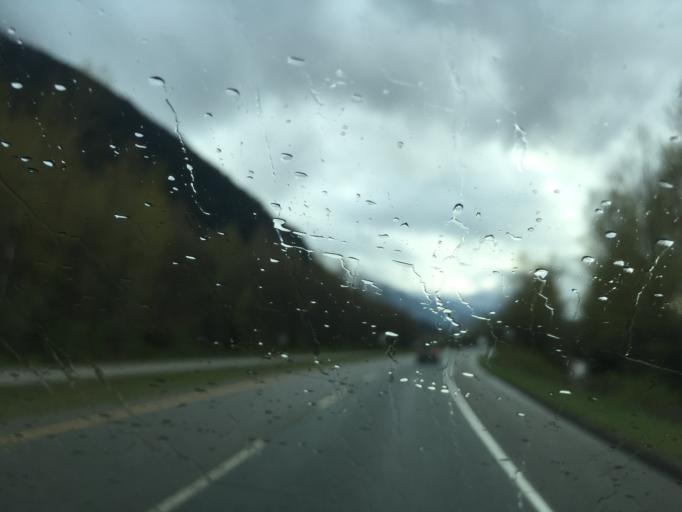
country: CA
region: British Columbia
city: Agassiz
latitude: 49.2846
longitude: -121.6694
